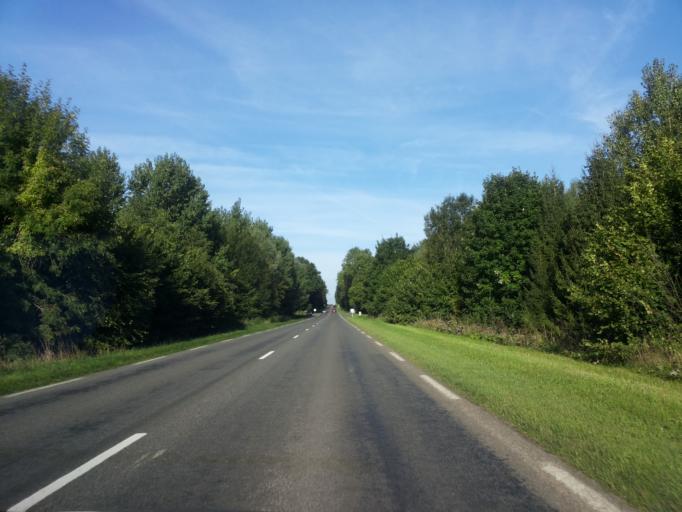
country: FR
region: Picardie
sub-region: Departement de l'Aisne
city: Crepy
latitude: 49.6217
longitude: 3.4498
